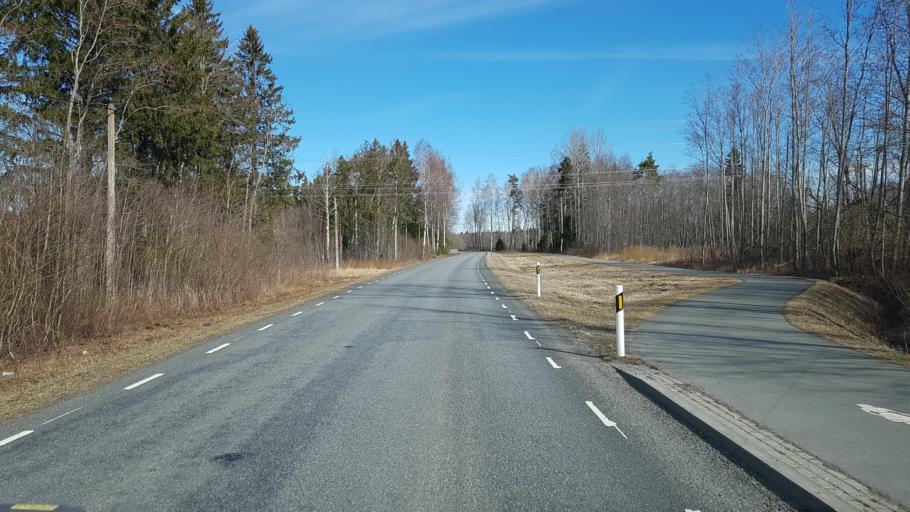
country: EE
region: Harju
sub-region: Nissi vald
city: Riisipere
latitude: 59.2338
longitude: 24.2446
